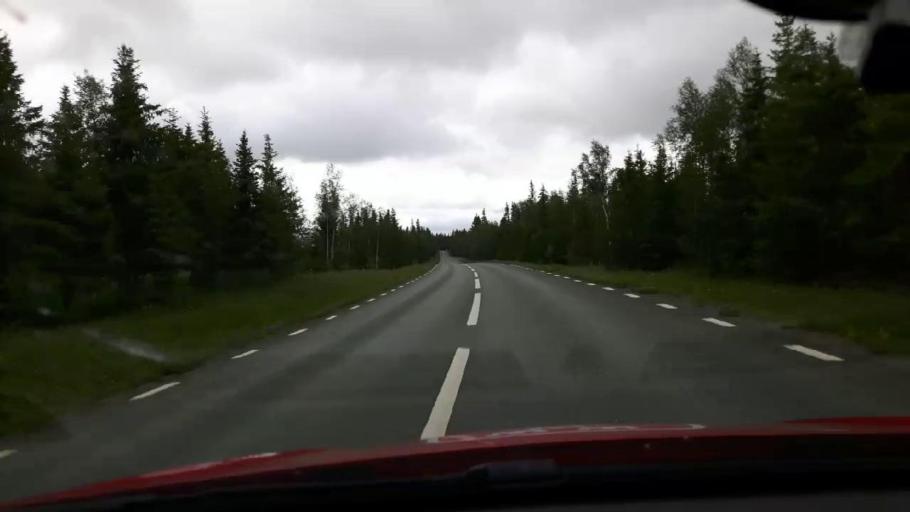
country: SE
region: Jaemtland
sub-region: Are Kommun
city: Are
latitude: 63.3538
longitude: 12.5914
